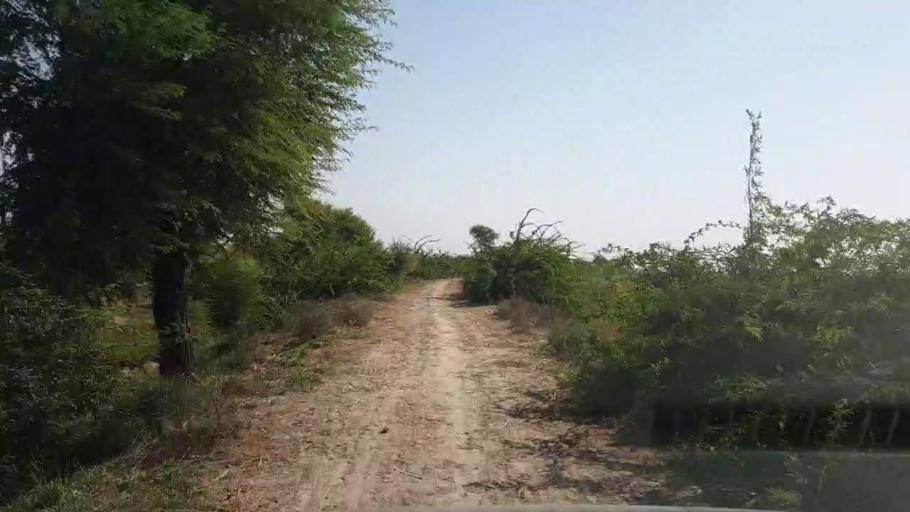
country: PK
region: Sindh
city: Kadhan
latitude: 24.6244
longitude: 68.9949
